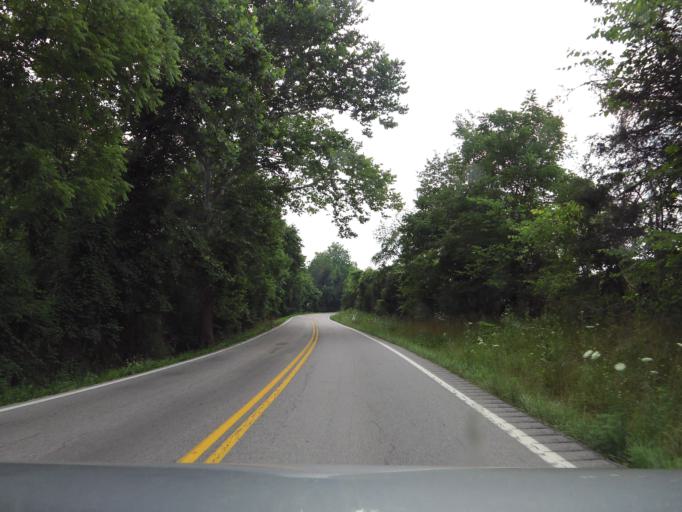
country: US
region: Kentucky
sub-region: Robertson County
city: Mount Olivet
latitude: 38.4914
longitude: -84.1148
